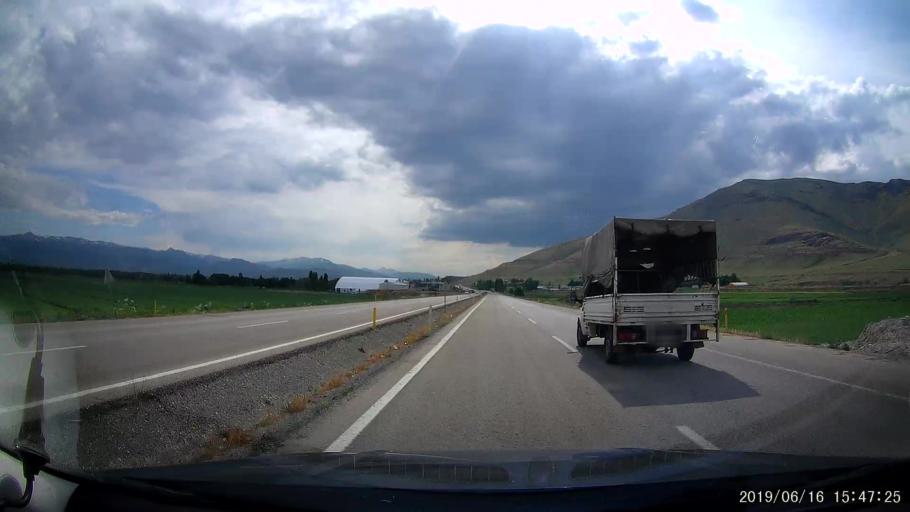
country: TR
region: Erzurum
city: Pasinler
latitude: 39.9885
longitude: 41.7214
